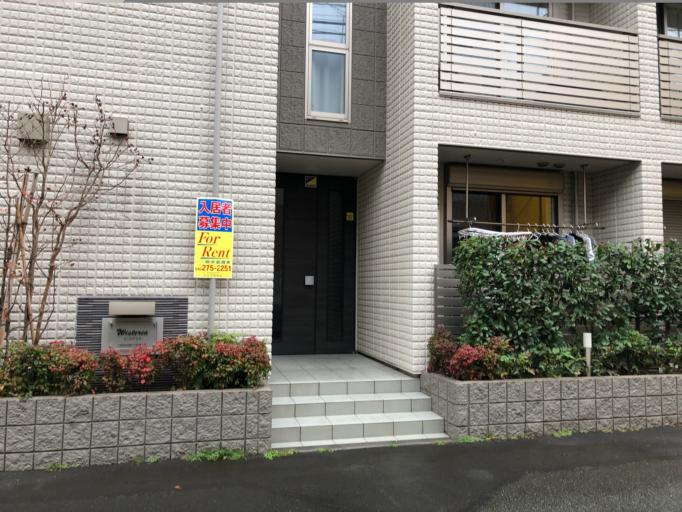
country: JP
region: Kanagawa
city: Minami-rinkan
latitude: 35.5067
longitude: 139.4433
